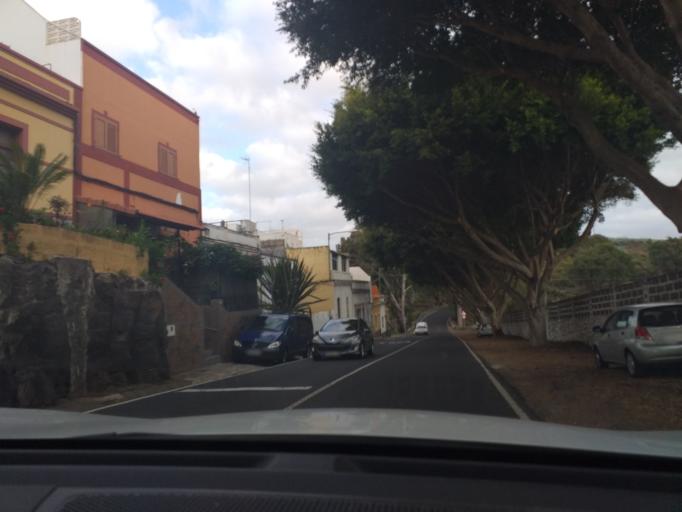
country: ES
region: Canary Islands
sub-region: Provincia de Las Palmas
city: Arucas
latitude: 28.1010
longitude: -15.4867
